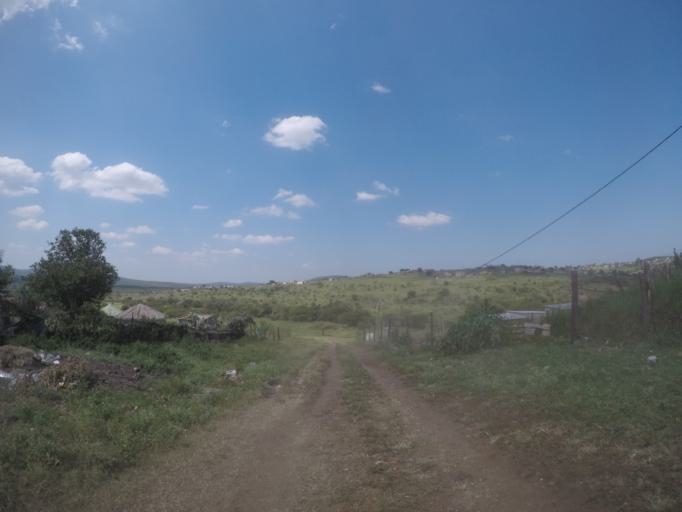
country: ZA
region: KwaZulu-Natal
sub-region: uThungulu District Municipality
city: Empangeni
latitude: -28.5912
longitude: 31.7428
